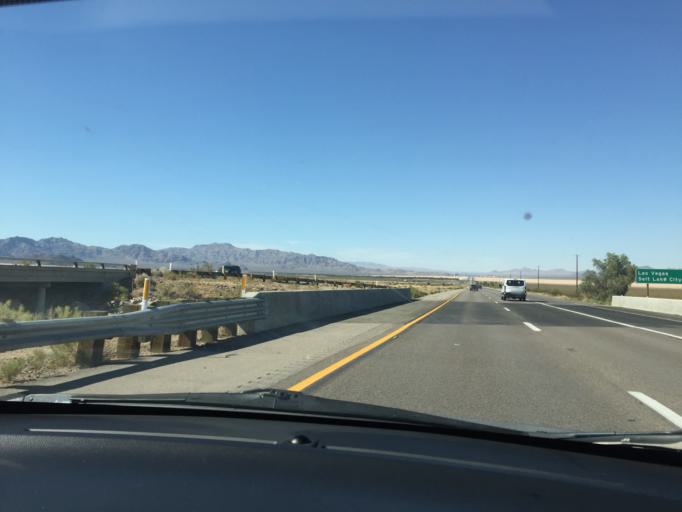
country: US
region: Nevada
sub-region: Clark County
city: Sandy Valley
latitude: 35.5130
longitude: -115.4315
